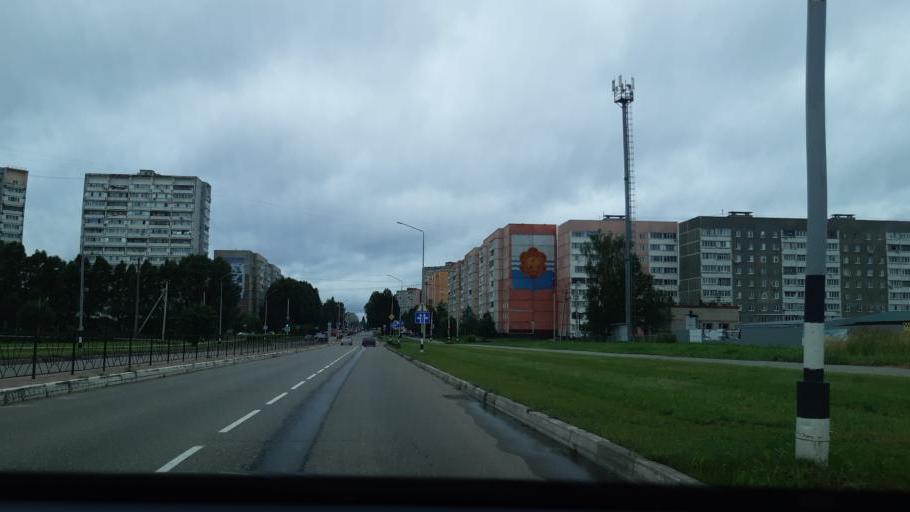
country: RU
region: Smolensk
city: Desnogorsk
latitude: 54.1461
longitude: 33.2825
